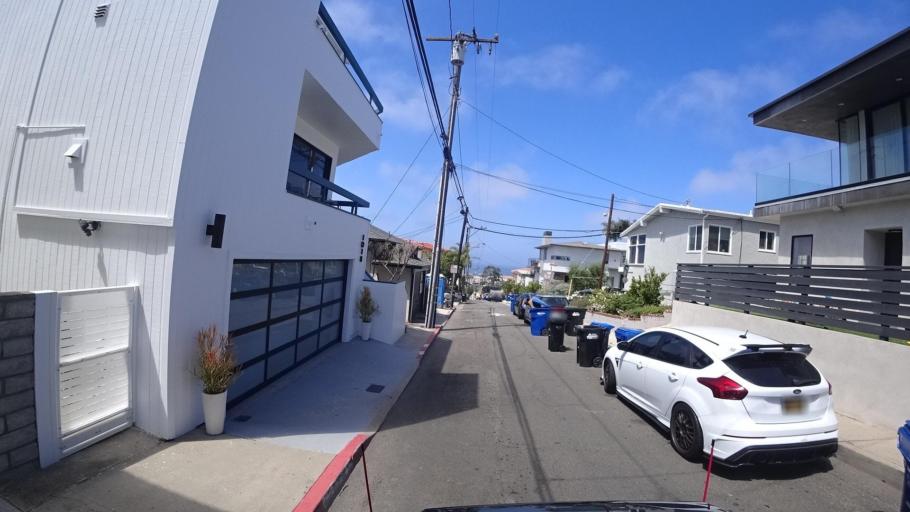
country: US
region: California
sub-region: Los Angeles County
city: Hermosa Beach
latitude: 33.8612
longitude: -118.3893
